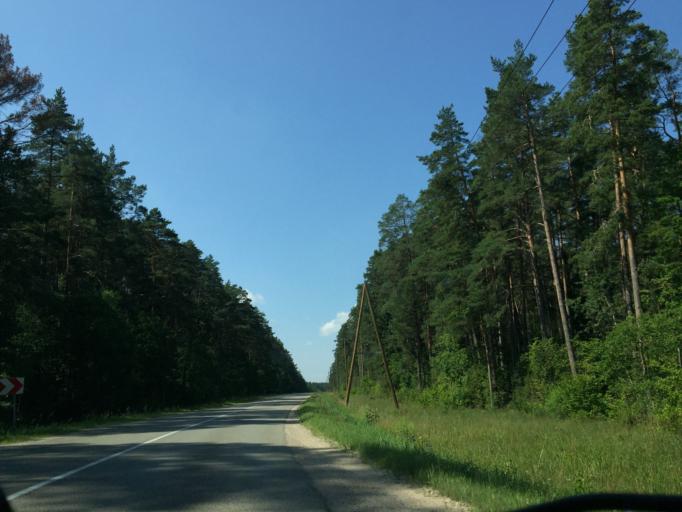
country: LV
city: Tervete
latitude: 56.4896
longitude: 23.4353
